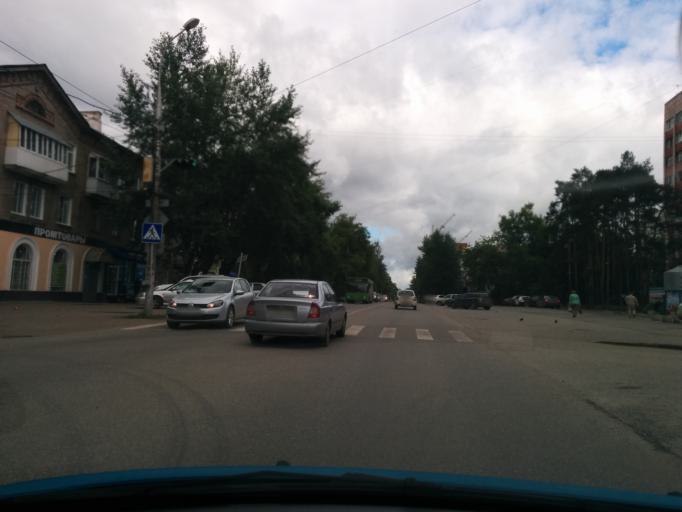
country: RU
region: Perm
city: Kondratovo
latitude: 58.0258
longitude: 56.0152
